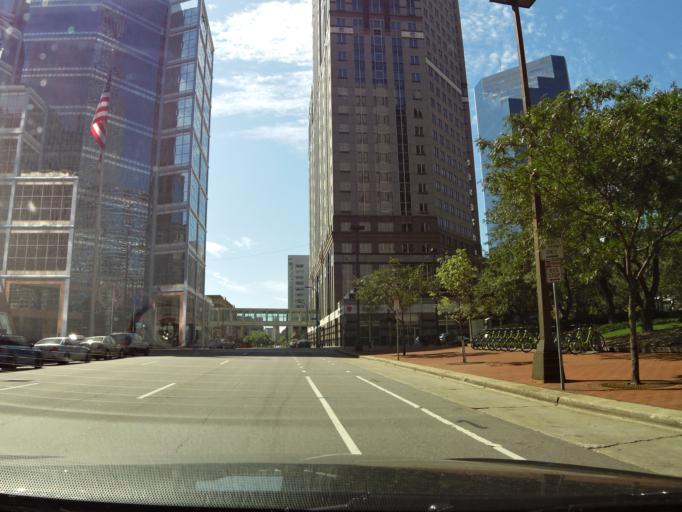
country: US
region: Minnesota
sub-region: Hennepin County
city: Minneapolis
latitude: 44.9750
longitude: -93.2662
